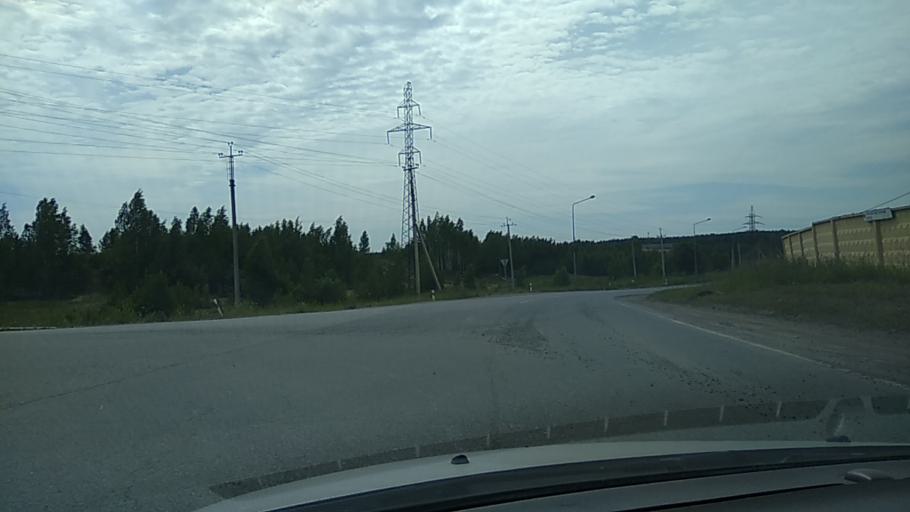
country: RU
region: Sverdlovsk
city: Verkhnyaya Pyshma
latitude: 56.9528
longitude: 60.5853
